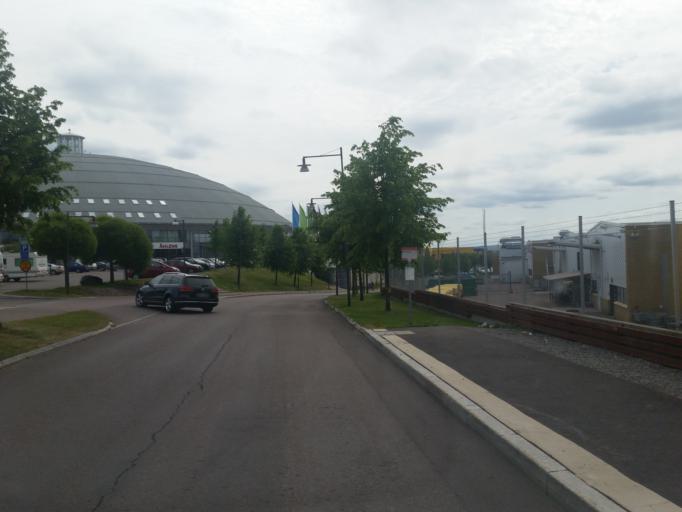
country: SE
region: Dalarna
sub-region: Borlange Kommun
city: Borlaenge
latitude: 60.4851
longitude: 15.4144
